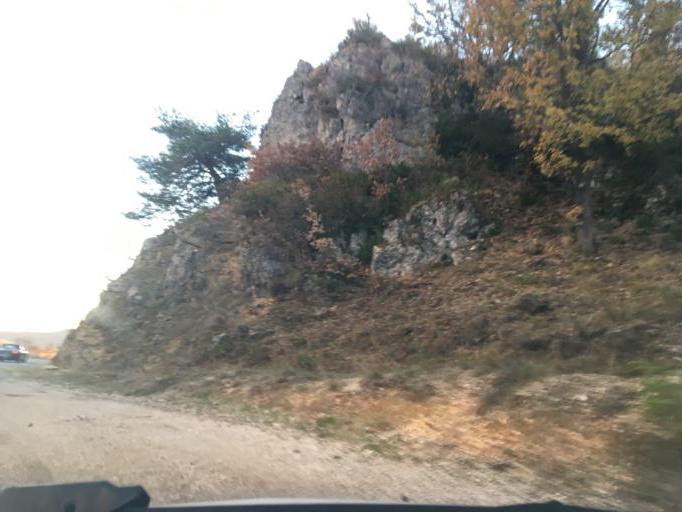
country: FR
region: Provence-Alpes-Cote d'Azur
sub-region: Departement du Var
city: Montferrat
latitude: 43.6968
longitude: 6.5038
